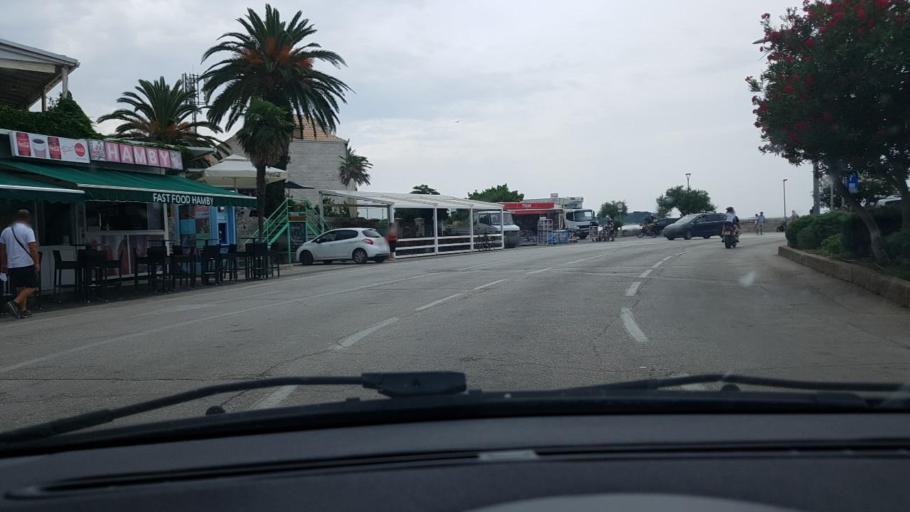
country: HR
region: Dubrovacko-Neretvanska
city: Orebic
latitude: 42.9744
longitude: 17.1761
